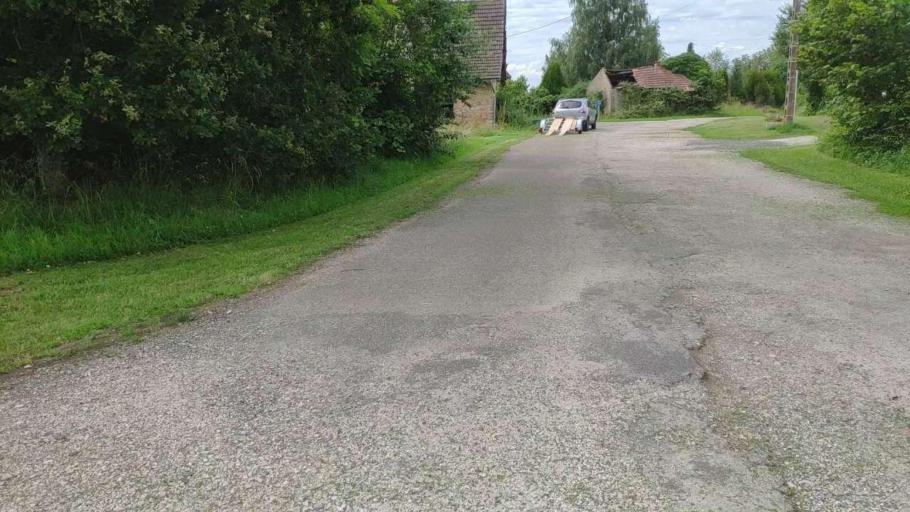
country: FR
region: Franche-Comte
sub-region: Departement du Jura
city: Chaussin
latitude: 46.8703
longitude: 5.4276
